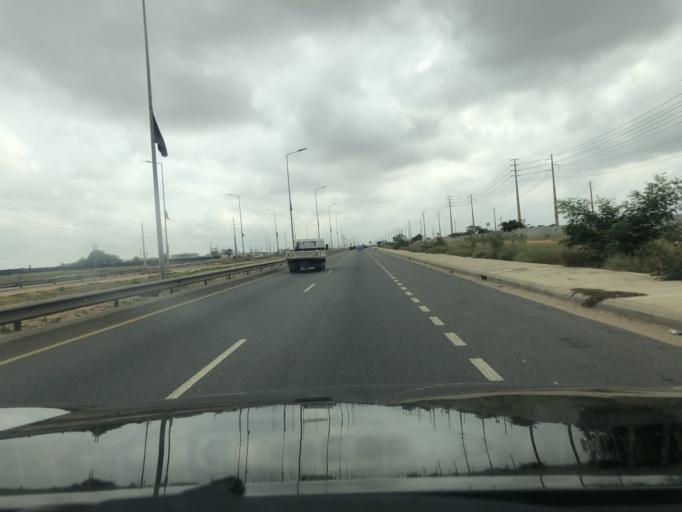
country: AO
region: Luanda
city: Luanda
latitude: -8.9622
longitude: 13.2567
